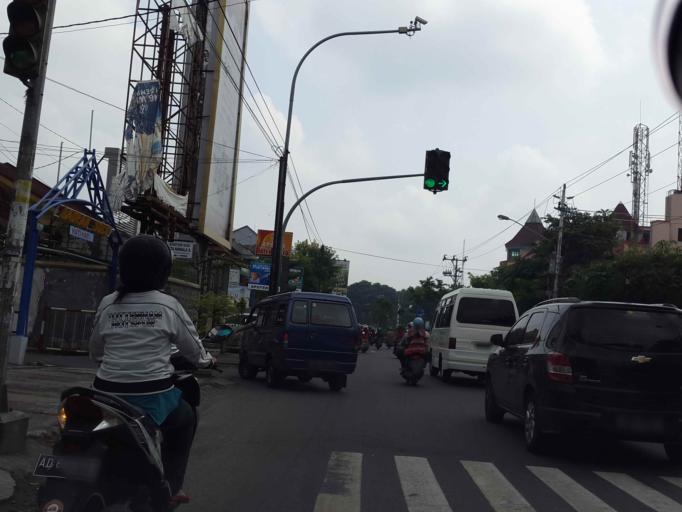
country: ID
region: Central Java
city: Surakarta
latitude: -7.5607
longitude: 110.8073
